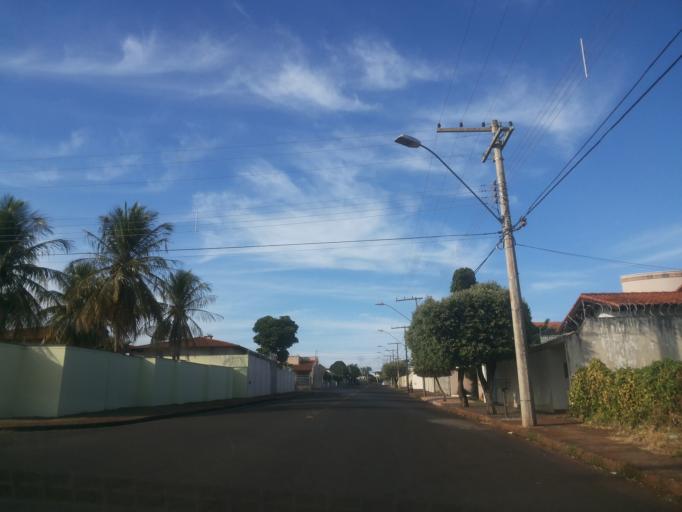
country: BR
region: Minas Gerais
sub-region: Ituiutaba
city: Ituiutaba
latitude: -18.9855
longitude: -49.4612
